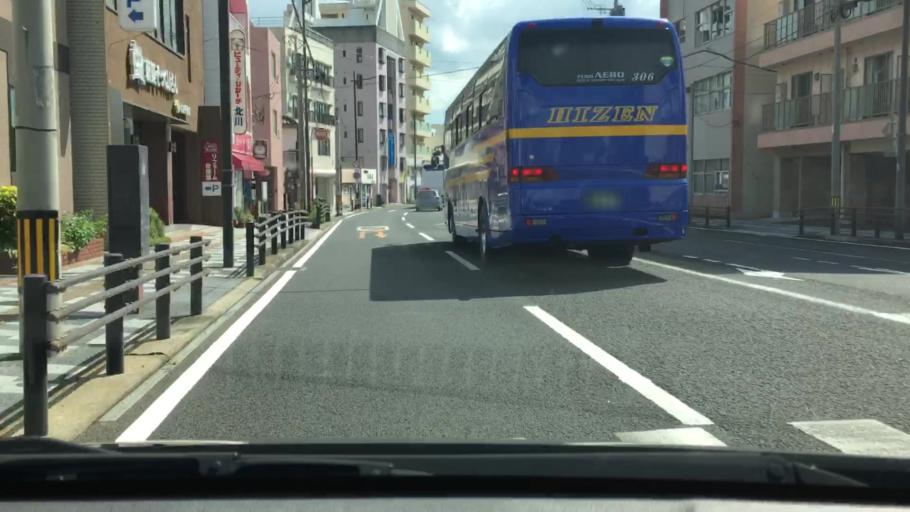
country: JP
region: Nagasaki
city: Sasebo
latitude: 33.1849
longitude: 129.7183
